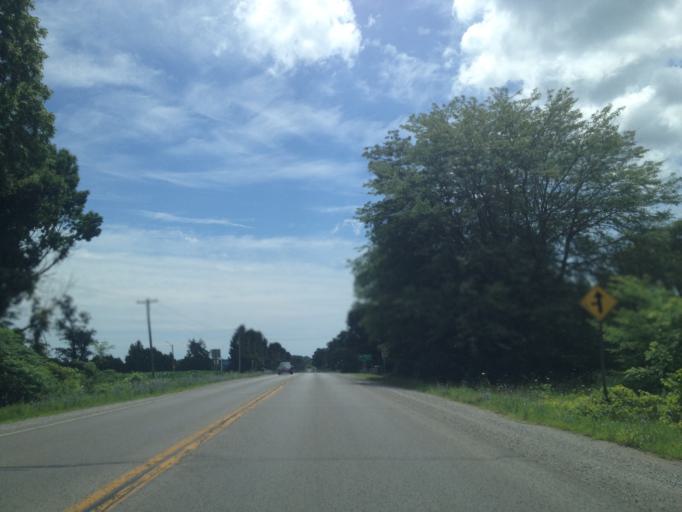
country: CA
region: Ontario
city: Norfolk County
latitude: 42.7750
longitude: -80.2810
